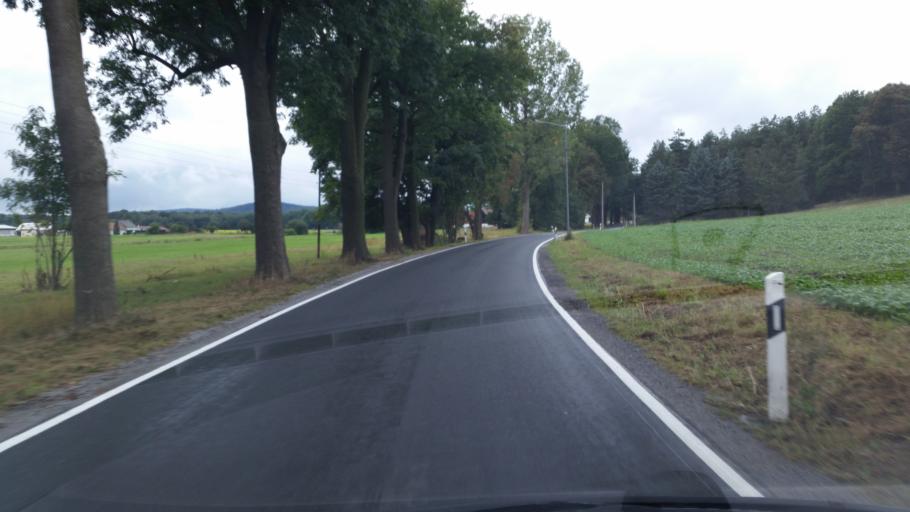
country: DE
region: Saxony
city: Kamenz
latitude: 51.2892
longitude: 14.0677
